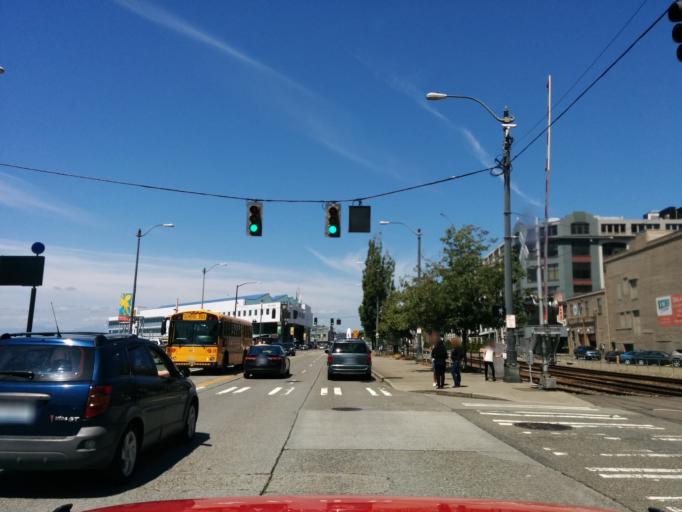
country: US
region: Washington
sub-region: King County
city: Seattle
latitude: 47.6129
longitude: -122.3509
